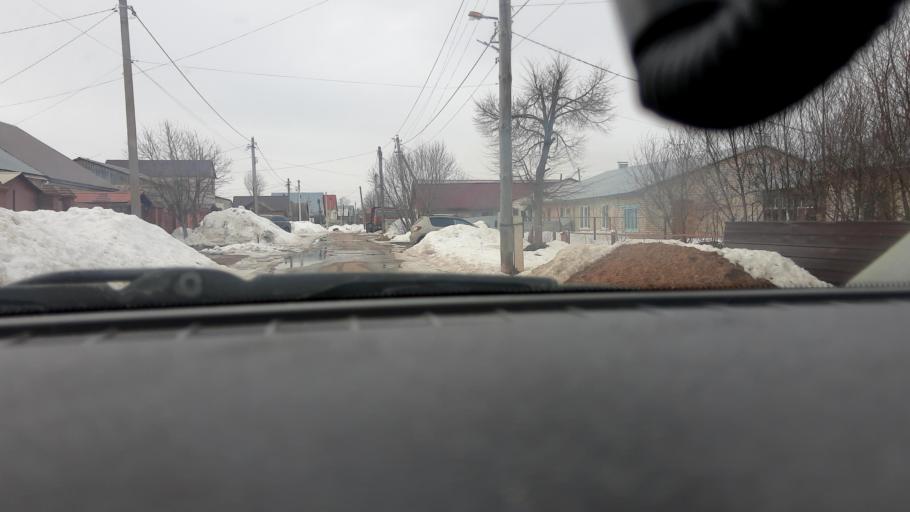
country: RU
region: Bashkortostan
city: Avdon
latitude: 54.6104
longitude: 55.8574
